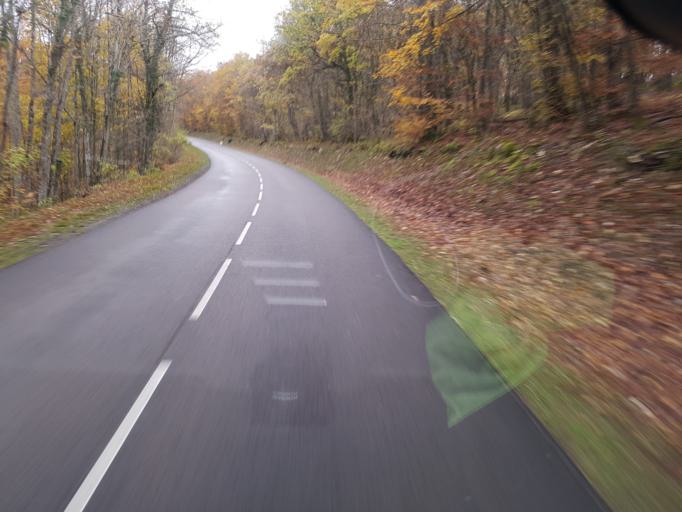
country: FR
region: Bourgogne
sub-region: Departement de la Cote-d'Or
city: Messigny-et-Vantoux
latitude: 47.5529
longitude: 4.9205
